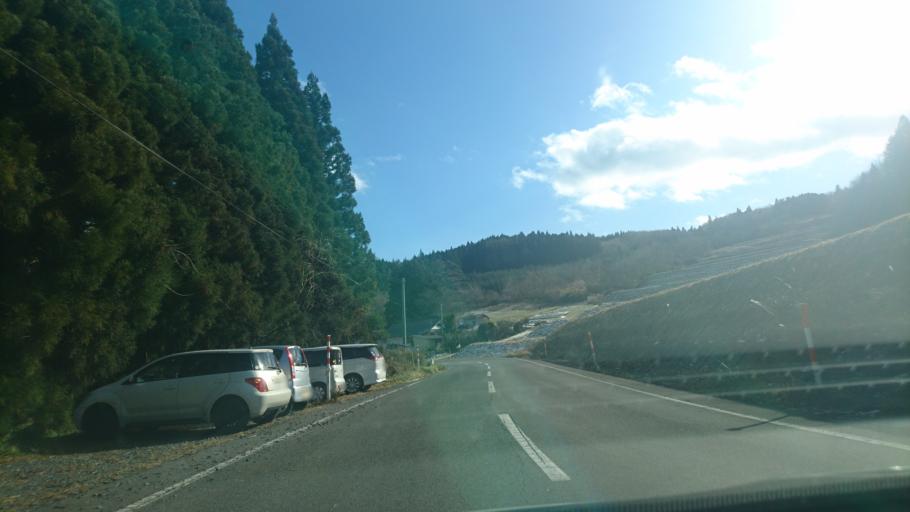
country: JP
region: Iwate
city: Ichinoseki
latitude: 38.9753
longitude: 141.3955
